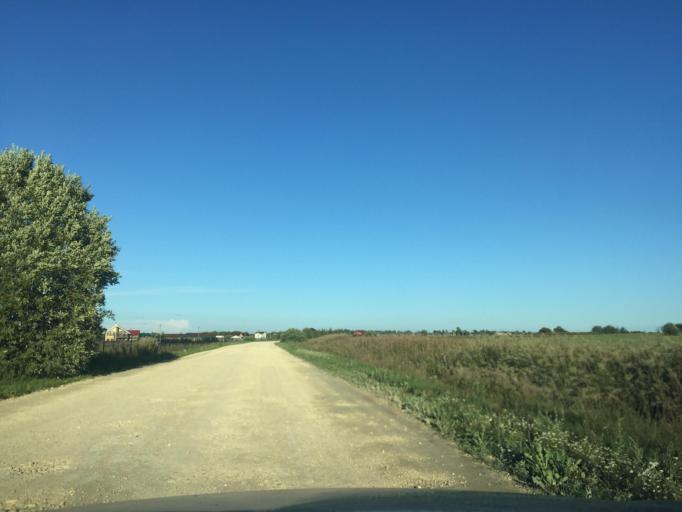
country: RU
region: Leningrad
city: Rozhdestveno
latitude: 59.3326
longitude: 30.0079
